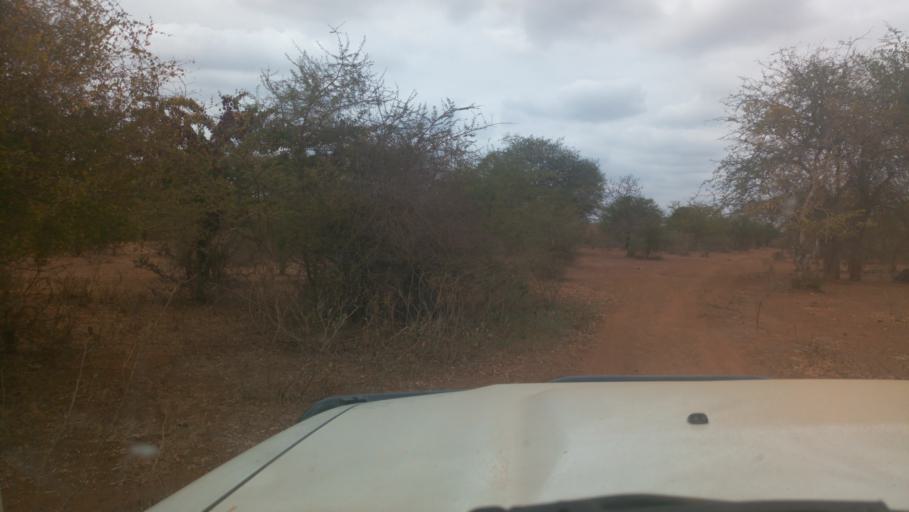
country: KE
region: Makueni
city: Wote
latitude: -1.7834
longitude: 37.9166
